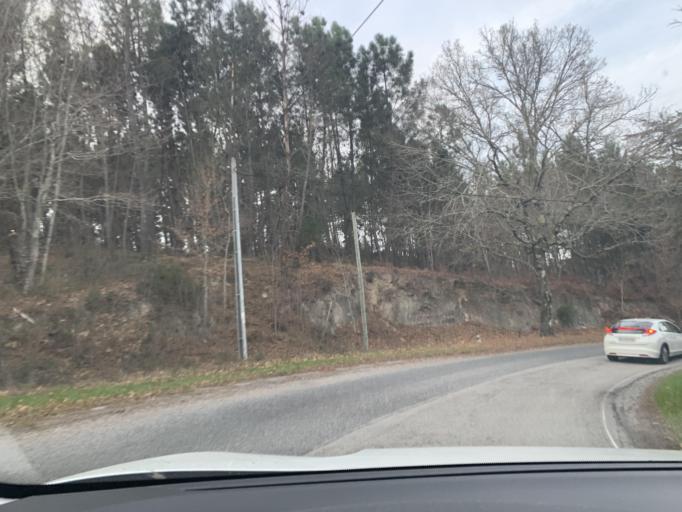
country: PT
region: Viseu
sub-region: Viseu
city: Viseu
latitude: 40.5977
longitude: -7.9944
